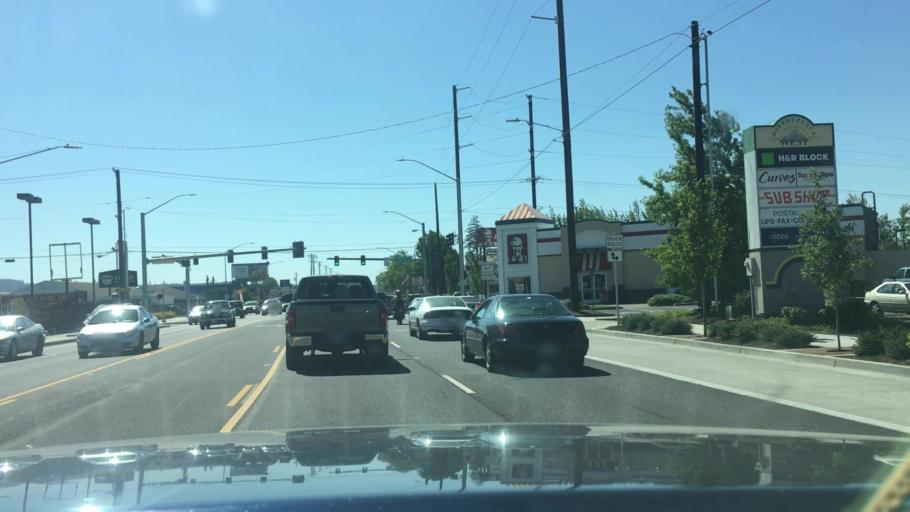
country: US
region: Oregon
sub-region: Lane County
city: Eugene
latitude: 44.0480
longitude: -123.1395
